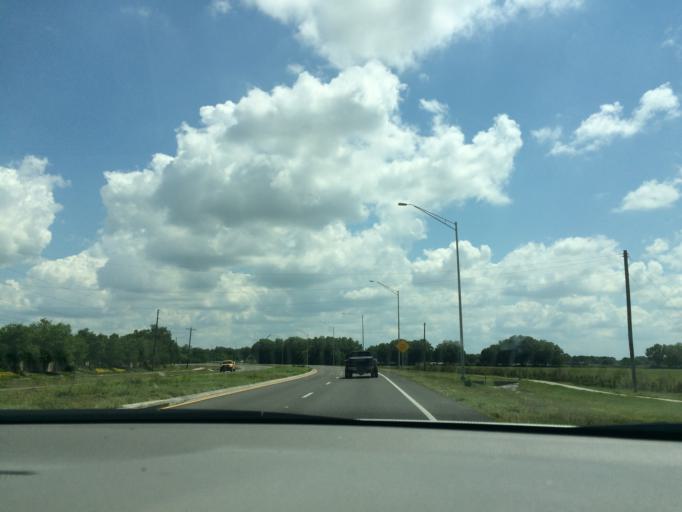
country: US
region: Florida
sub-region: Manatee County
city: Ellenton
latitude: 27.4791
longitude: -82.4037
